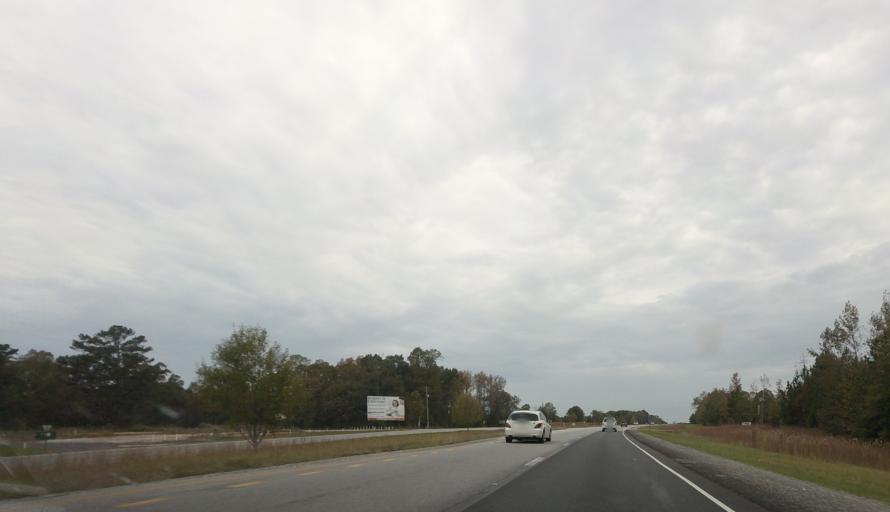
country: US
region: Alabama
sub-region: Lee County
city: Opelika
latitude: 32.6247
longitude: -85.2777
